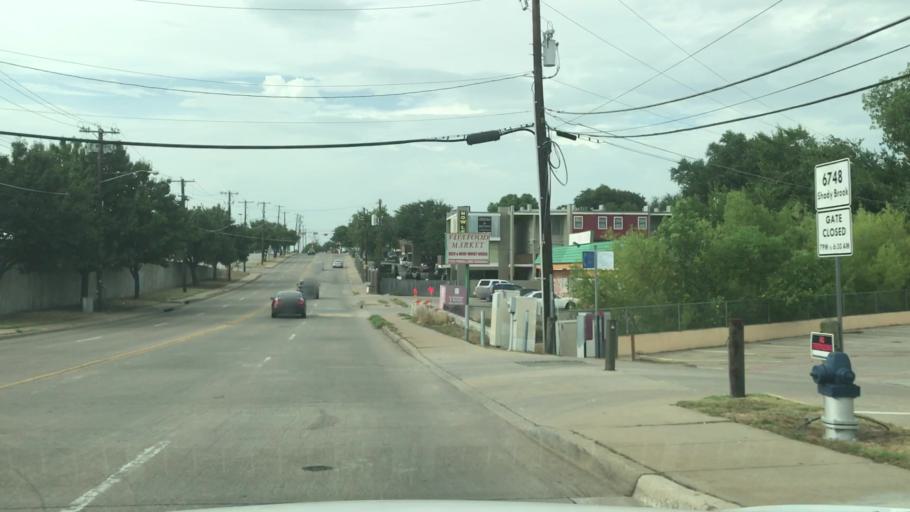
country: US
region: Texas
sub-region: Dallas County
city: University Park
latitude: 32.8676
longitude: -96.7634
